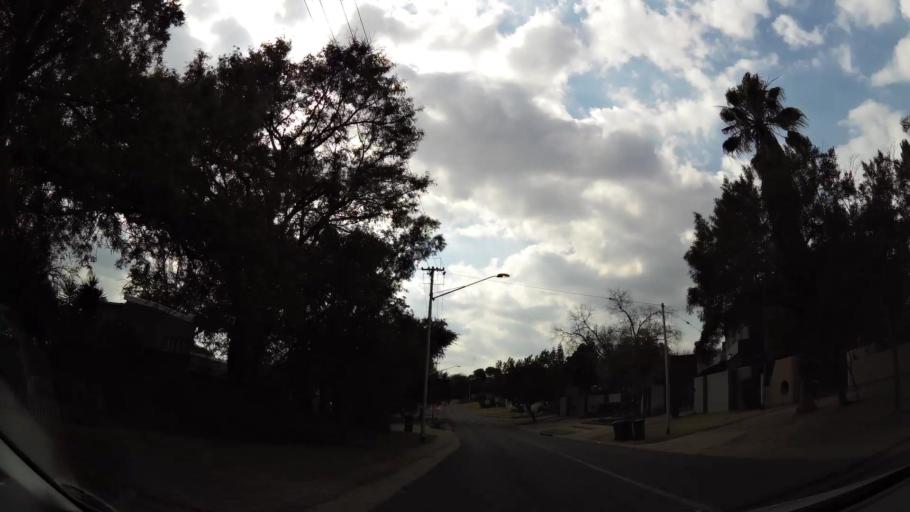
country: ZA
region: Gauteng
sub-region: City of Tshwane Metropolitan Municipality
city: Pretoria
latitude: -25.7613
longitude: 28.2922
